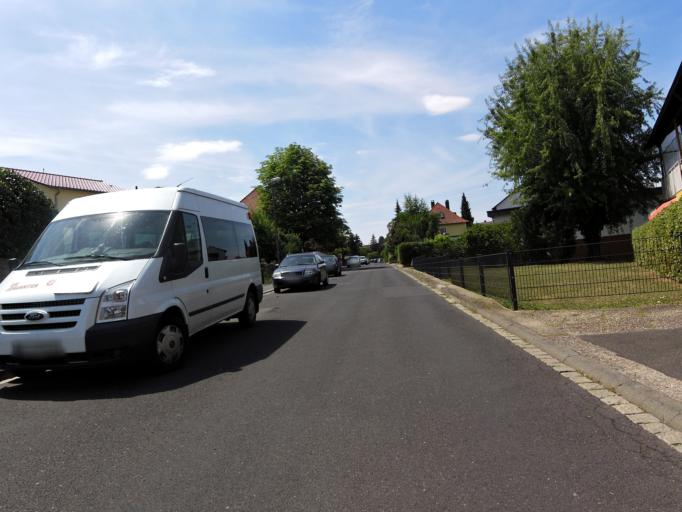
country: DE
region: Bavaria
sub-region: Regierungsbezirk Unterfranken
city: Randersacker
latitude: 49.7592
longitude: 9.9526
